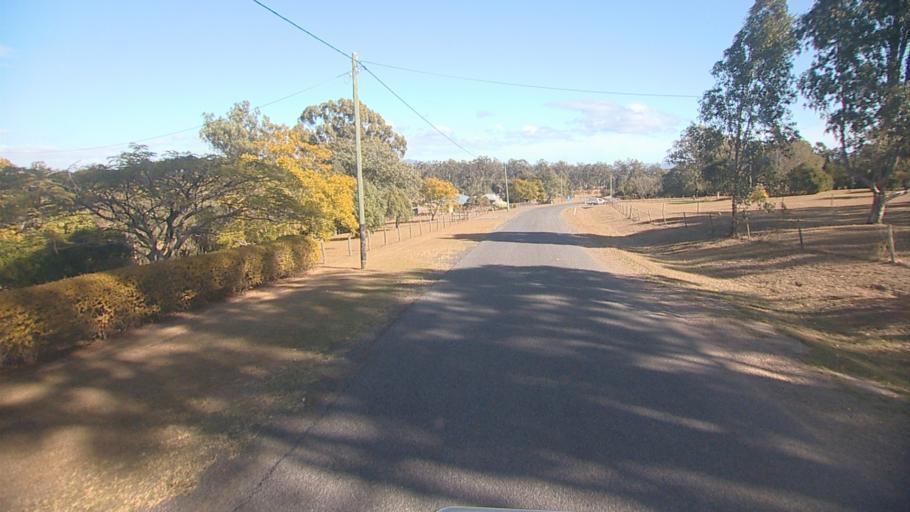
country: AU
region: Queensland
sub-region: Logan
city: Cedar Vale
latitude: -27.8765
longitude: 152.9790
